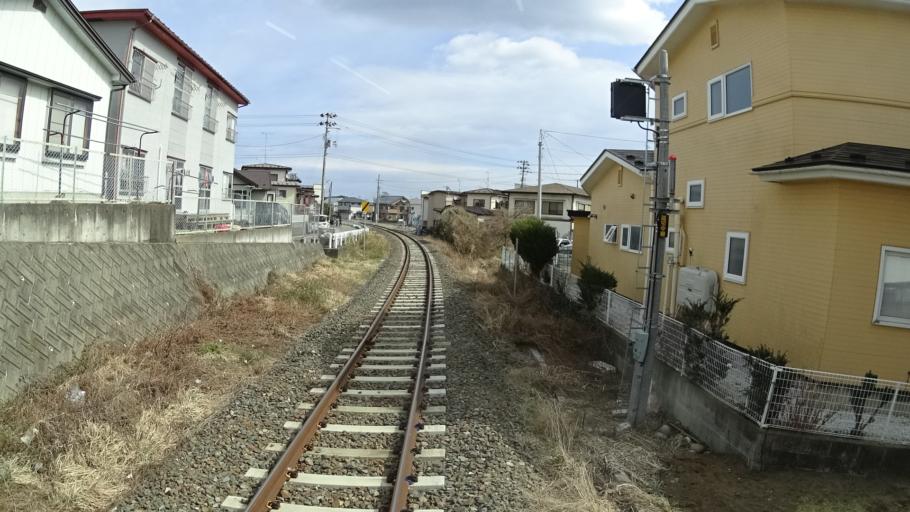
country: JP
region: Iwate
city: Miyako
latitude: 39.6267
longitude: 141.9592
